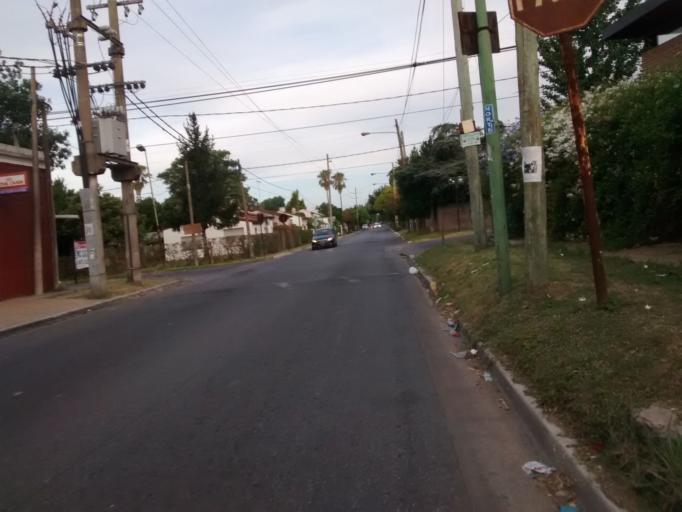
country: AR
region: Buenos Aires
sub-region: Partido de La Plata
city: La Plata
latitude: -34.8923
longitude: -58.0355
